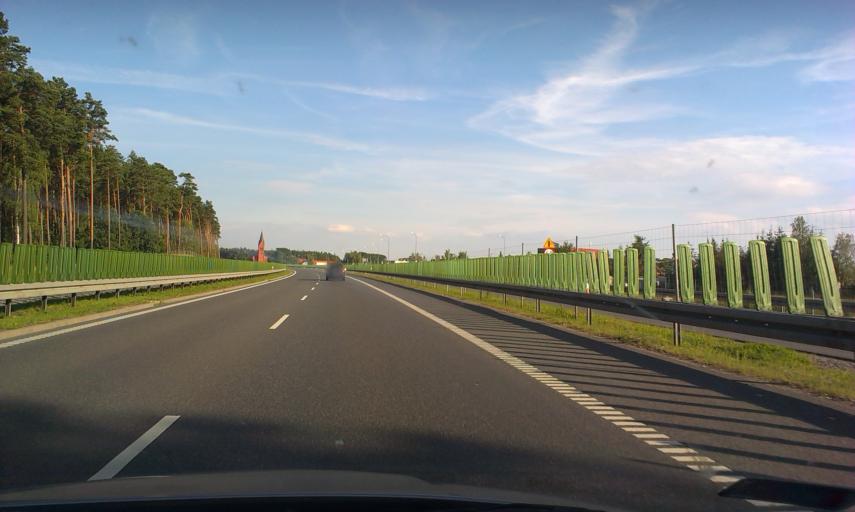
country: PL
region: Kujawsko-Pomorskie
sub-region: Powiat bydgoski
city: Biale Blota
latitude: 53.0775
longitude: 17.9129
